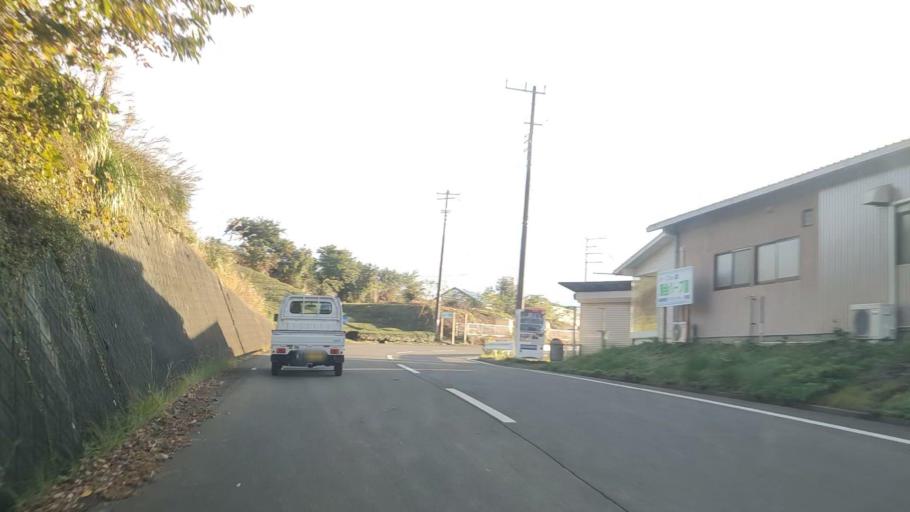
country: JP
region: Shizuoka
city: Mishima
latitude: 35.1315
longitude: 138.9727
